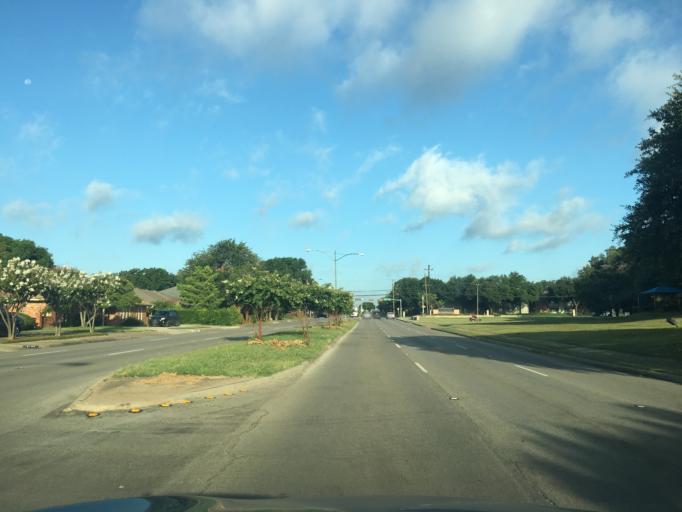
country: US
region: Texas
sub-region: Dallas County
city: Highland Park
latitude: 32.8510
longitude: -96.7586
